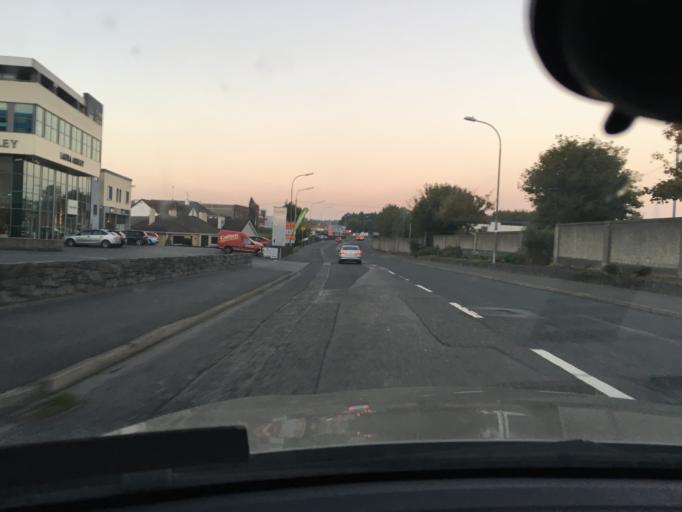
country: IE
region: Connaught
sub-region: County Galway
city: Gaillimh
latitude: 53.2838
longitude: -9.0356
